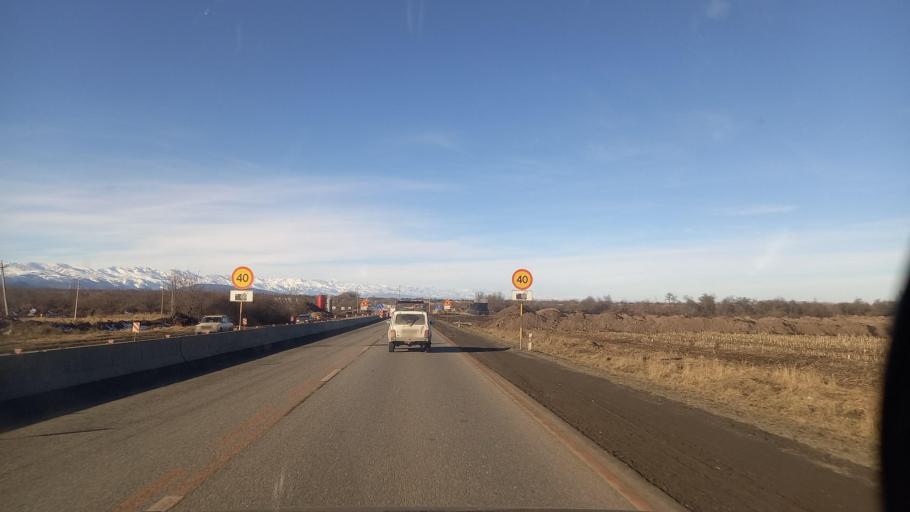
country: RU
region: North Ossetia
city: Gizel'
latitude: 43.0273
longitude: 44.6096
